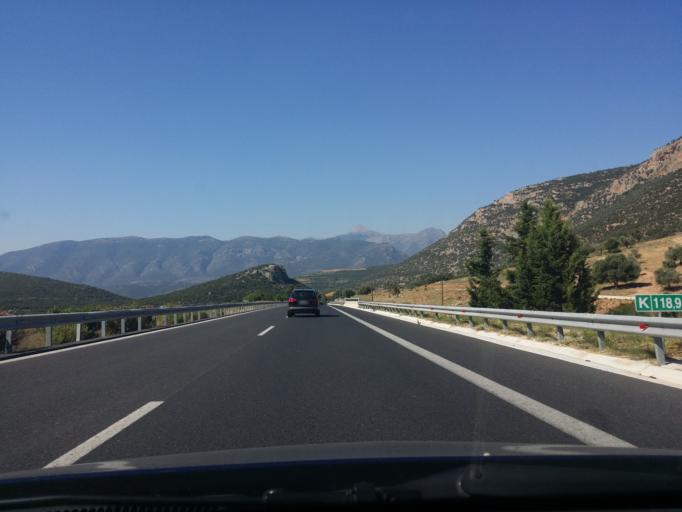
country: GR
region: Peloponnese
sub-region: Nomos Korinthias
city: Nemea
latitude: 37.7574
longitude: 22.6355
